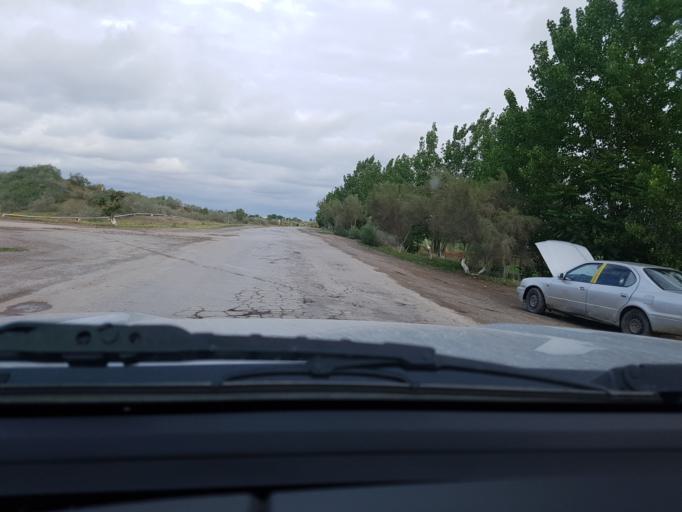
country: TM
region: Lebap
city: Atamyrat
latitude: 38.1131
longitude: 64.7324
